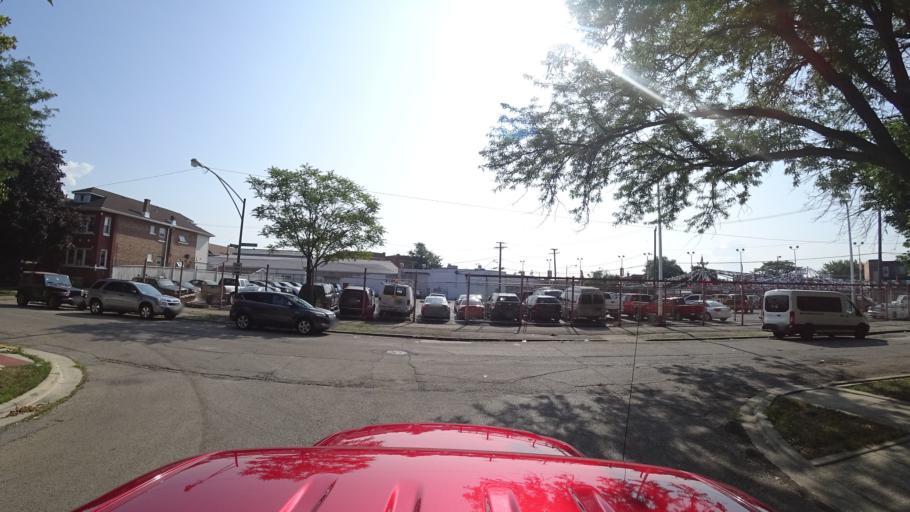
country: US
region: Illinois
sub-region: Cook County
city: Cicero
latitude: 41.8136
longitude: -87.7068
